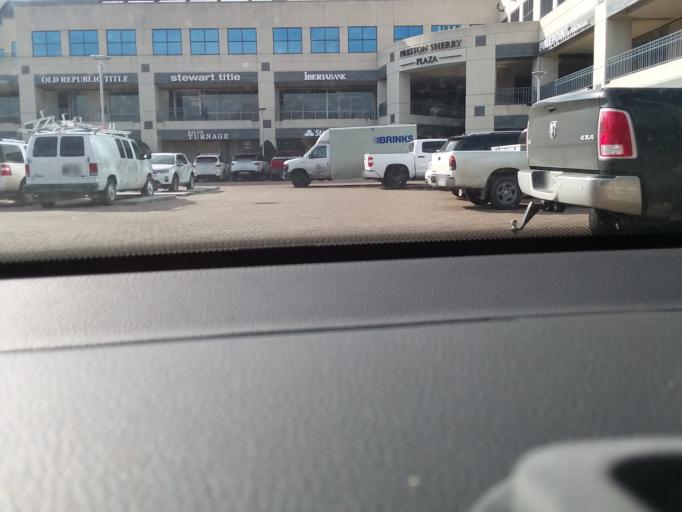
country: US
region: Texas
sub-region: Dallas County
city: University Park
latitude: 32.8626
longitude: -96.8042
